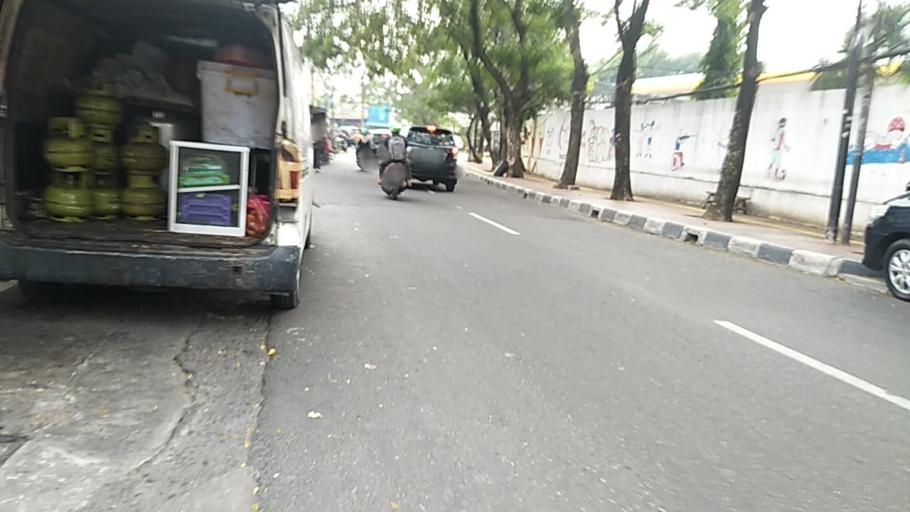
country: ID
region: Jakarta Raya
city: Jakarta
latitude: -6.2252
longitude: 106.8524
